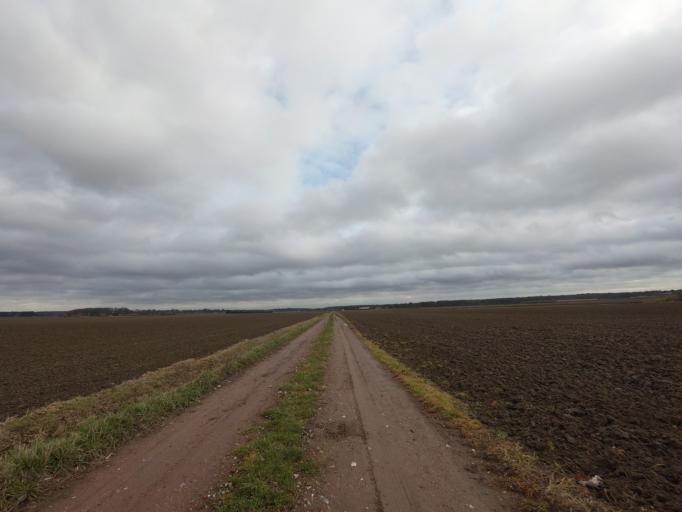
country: NL
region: North Brabant
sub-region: Gemeente Woensdrecht
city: Woensdrecht
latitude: 51.3784
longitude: 4.3168
